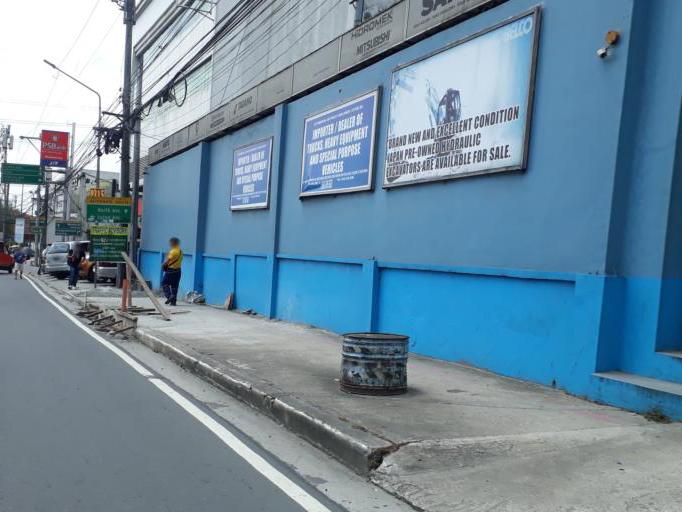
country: PH
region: Calabarzon
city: Bagong Pagasa
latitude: 14.6689
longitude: 121.0330
